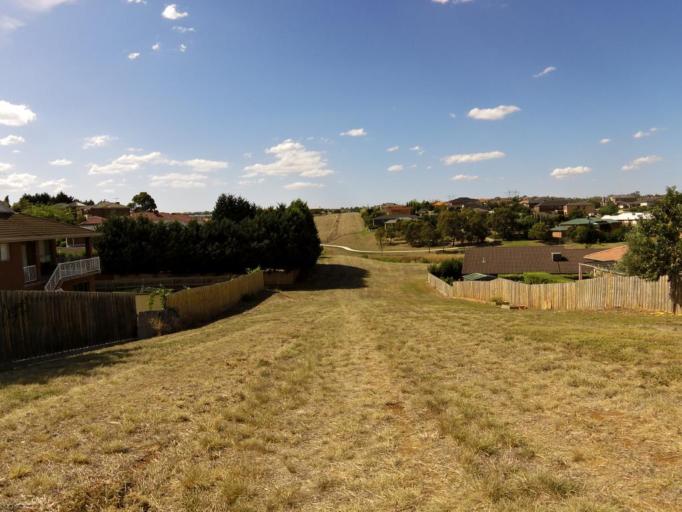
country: AU
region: Victoria
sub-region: Hume
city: Meadow Heights
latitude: -37.6559
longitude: 144.9041
